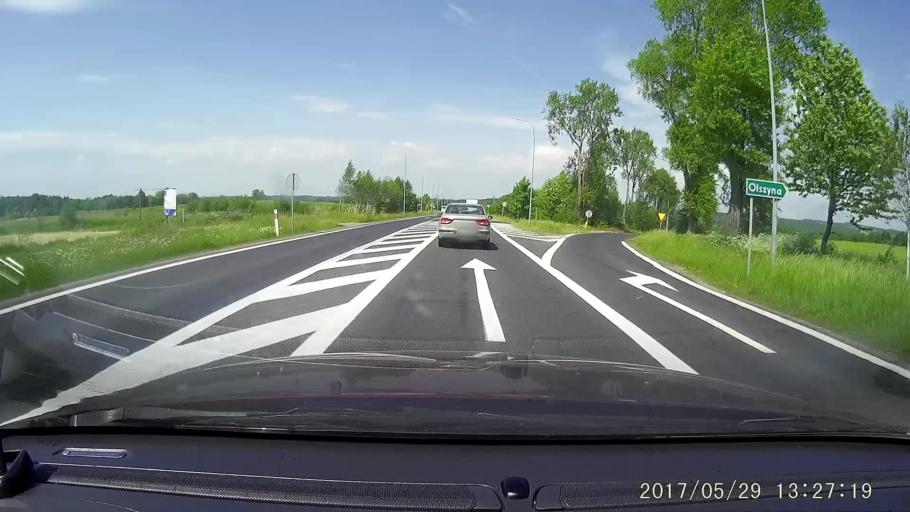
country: PL
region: Lower Silesian Voivodeship
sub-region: Powiat lubanski
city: Olszyna
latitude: 51.0534
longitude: 15.3728
